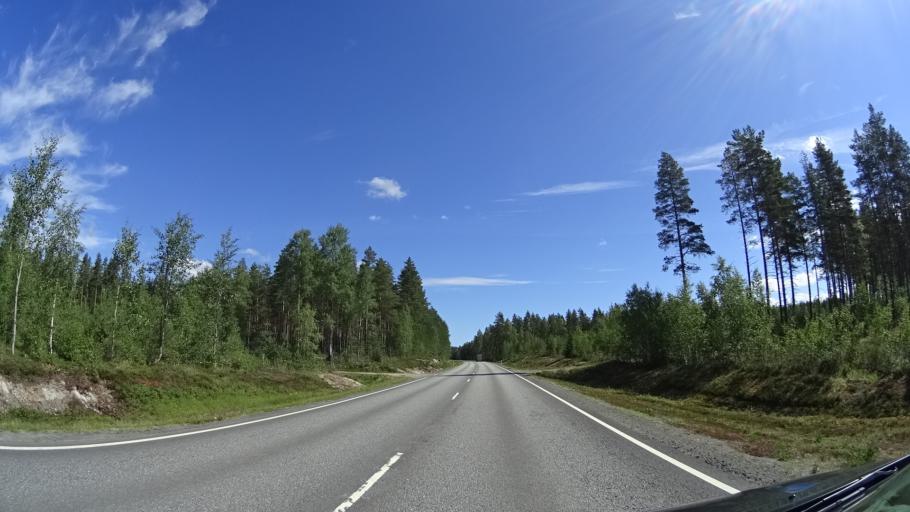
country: FI
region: Pirkanmaa
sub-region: Luoteis-Pirkanmaa
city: Kihnioe
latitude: 62.2231
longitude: 23.2837
